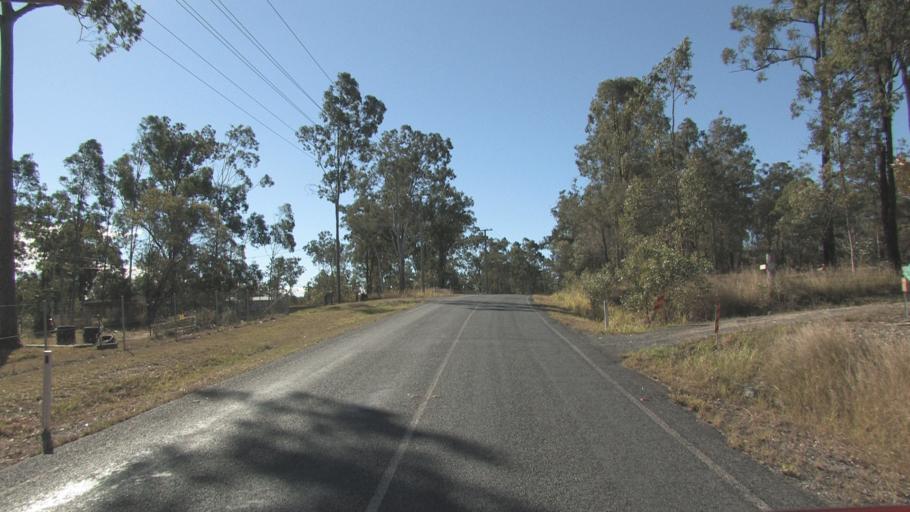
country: AU
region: Queensland
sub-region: Logan
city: Cedar Vale
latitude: -27.8259
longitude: 153.0539
